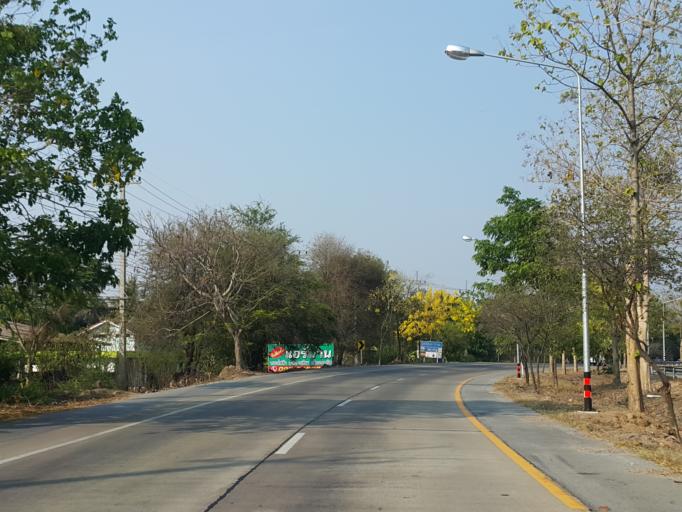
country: TH
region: Suphan Buri
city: Sam Chuk
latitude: 14.7872
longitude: 100.0895
